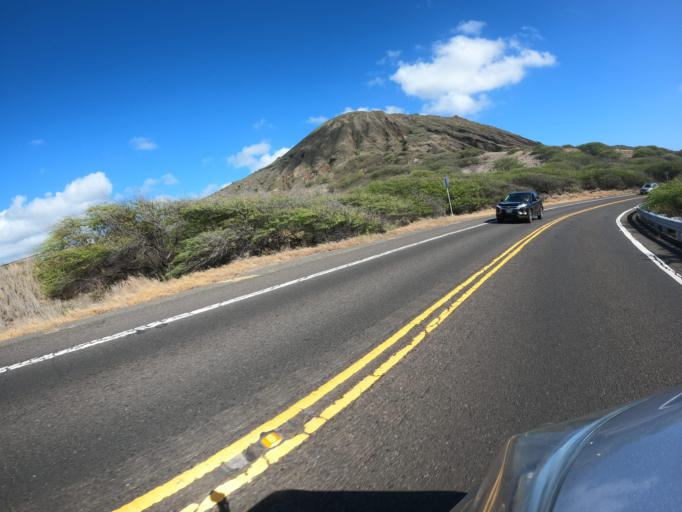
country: US
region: Hawaii
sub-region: Honolulu County
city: Waimanalo Beach
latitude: 21.2760
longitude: -157.6874
